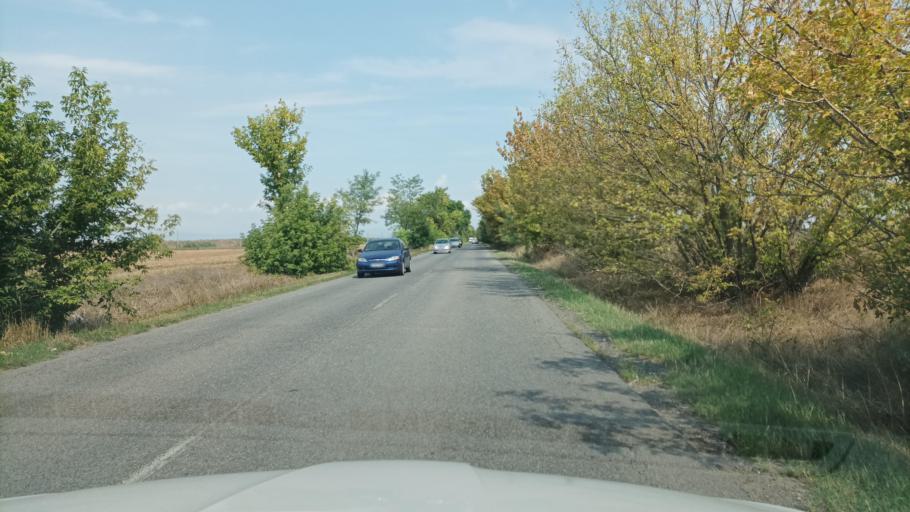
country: HU
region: Pest
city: Tura
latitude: 47.6294
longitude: 19.6263
